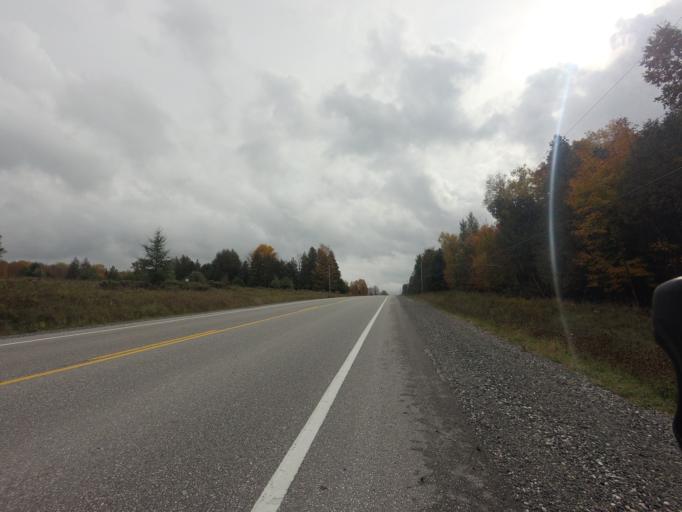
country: CA
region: Ontario
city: Perth
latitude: 45.1011
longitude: -76.4699
